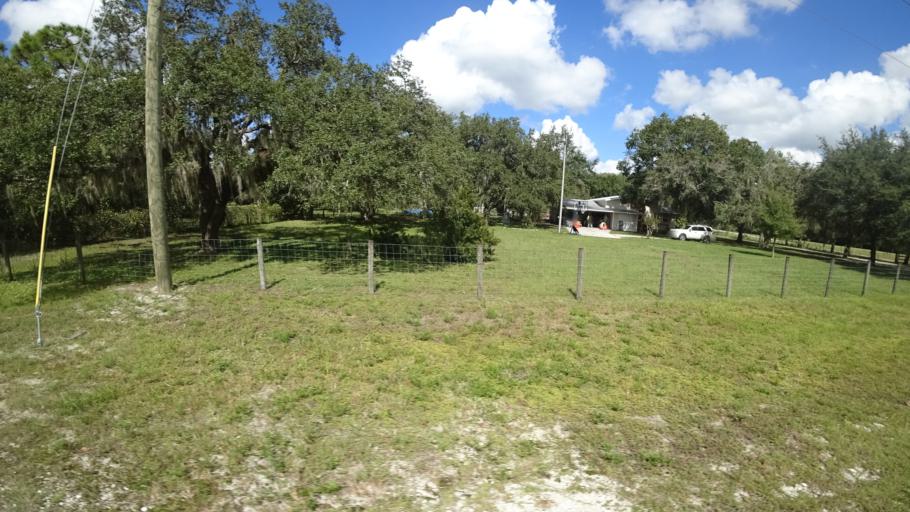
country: US
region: Florida
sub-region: Sarasota County
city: Lake Sarasota
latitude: 27.3509
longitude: -82.2396
